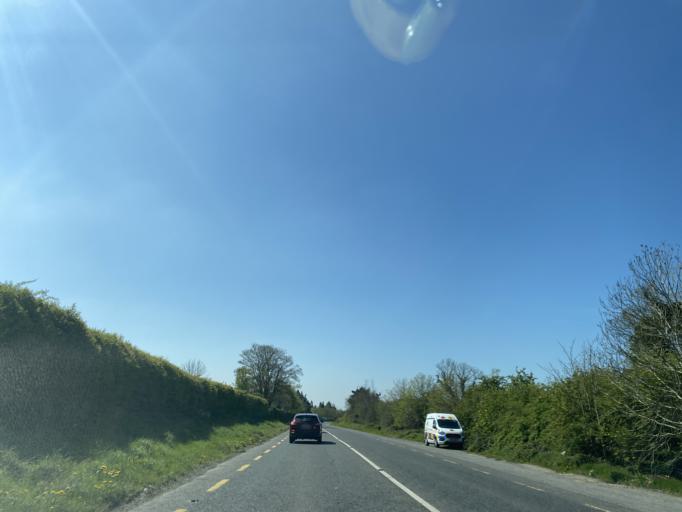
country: IE
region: Leinster
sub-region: Kildare
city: Maynooth
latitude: 53.3386
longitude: -6.6034
